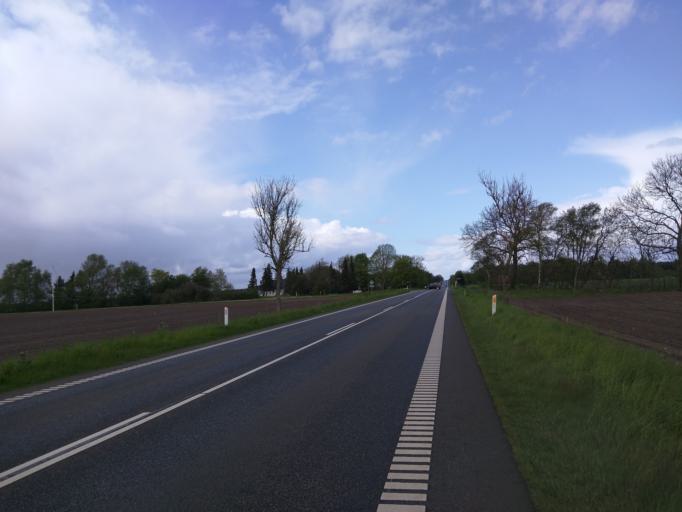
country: DK
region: Central Jutland
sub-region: Viborg Kommune
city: Viborg
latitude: 56.3756
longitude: 9.4413
